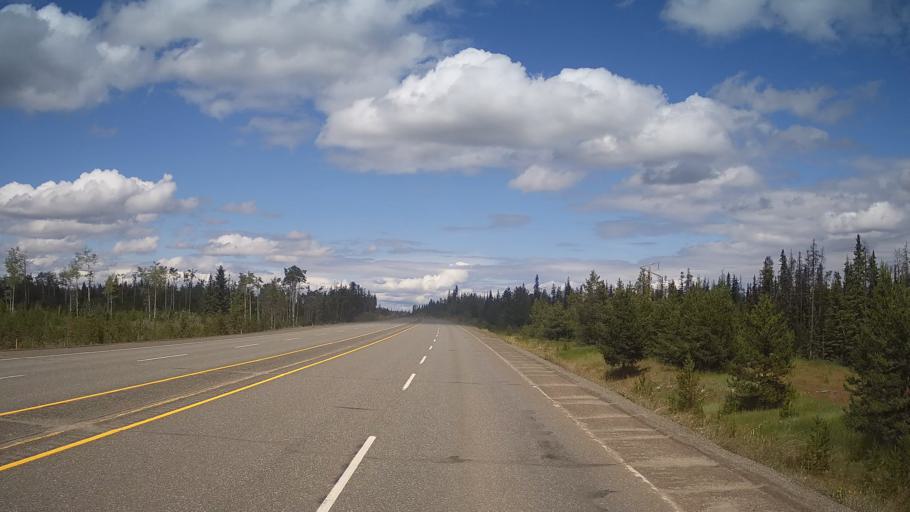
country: CA
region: British Columbia
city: Cache Creek
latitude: 51.5151
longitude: -121.3672
